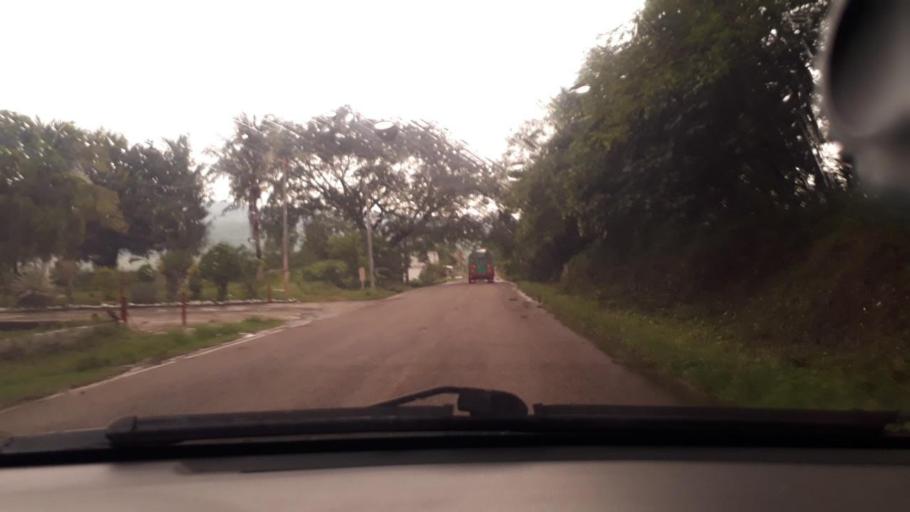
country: GT
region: Jutiapa
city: Comapa
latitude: 14.0546
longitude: -89.9366
